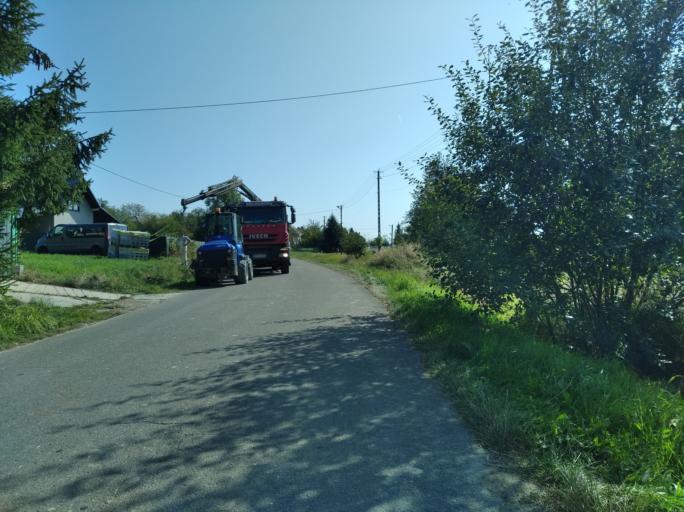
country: PL
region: Subcarpathian Voivodeship
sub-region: Powiat strzyzowski
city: Czudec
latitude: 49.9640
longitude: 21.8237
